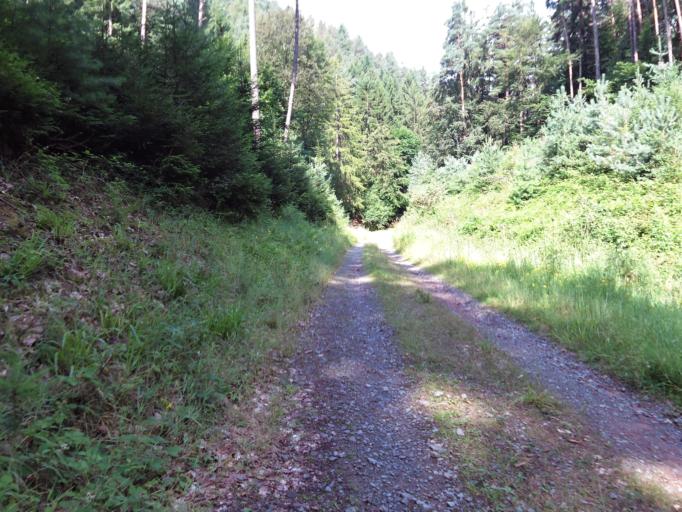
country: DE
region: Rheinland-Pfalz
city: Neidenfels
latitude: 49.4263
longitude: 8.0643
